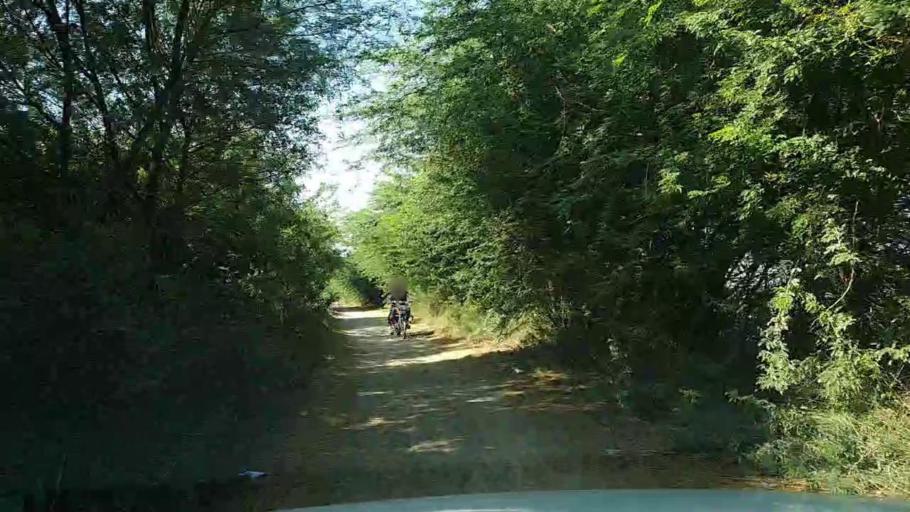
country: PK
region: Sindh
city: Mirpur Batoro
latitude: 24.6912
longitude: 68.1758
